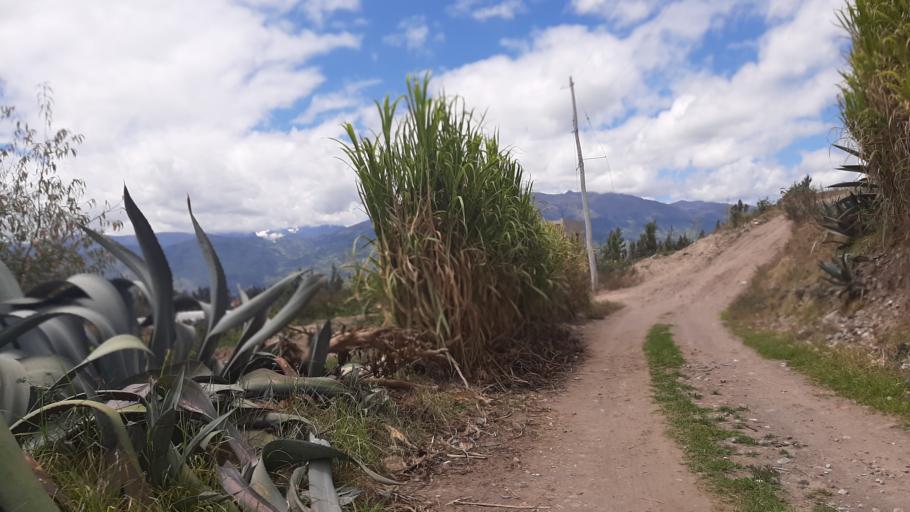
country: EC
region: Chimborazo
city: Riobamba
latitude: -1.6506
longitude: -78.6342
